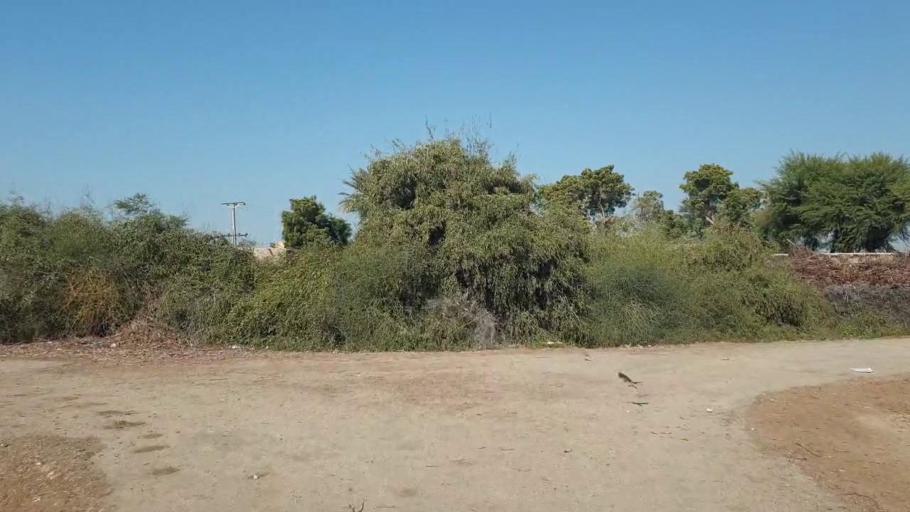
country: PK
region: Sindh
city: Shahdadpur
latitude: 25.9620
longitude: 68.6407
